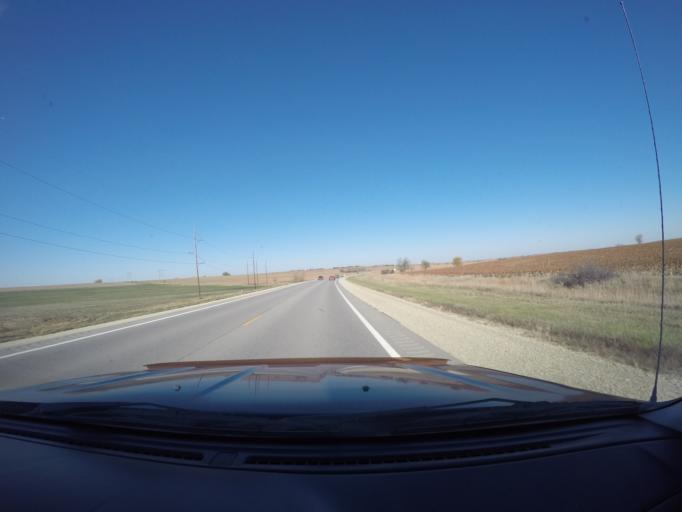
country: US
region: Kansas
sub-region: Riley County
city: Ogden
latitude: 39.2897
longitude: -96.7512
